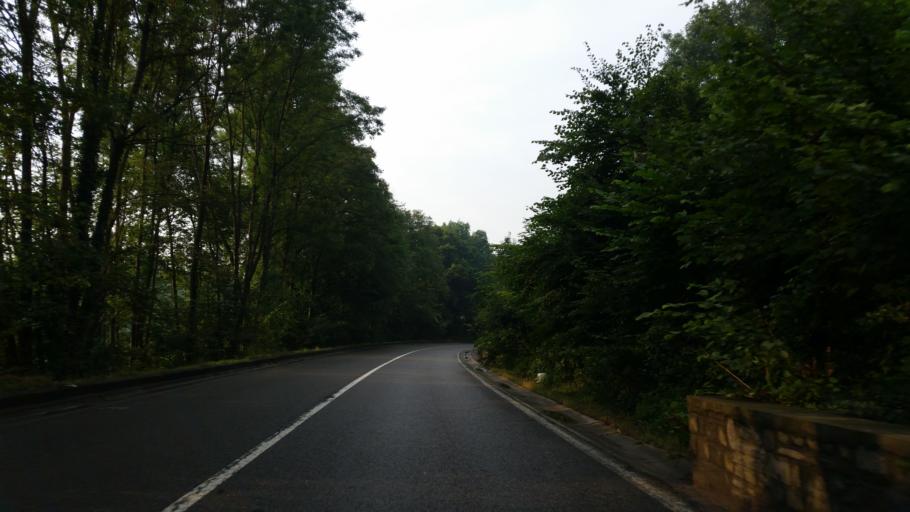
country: BE
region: Wallonia
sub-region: Province de Namur
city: Rochefort
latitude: 50.1454
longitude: 5.1947
